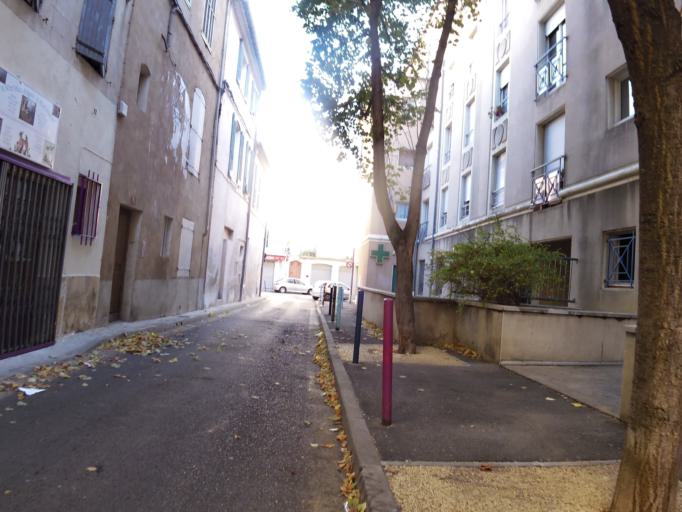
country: FR
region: Languedoc-Roussillon
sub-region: Departement du Gard
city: Nimes
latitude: 43.8415
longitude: 4.3609
